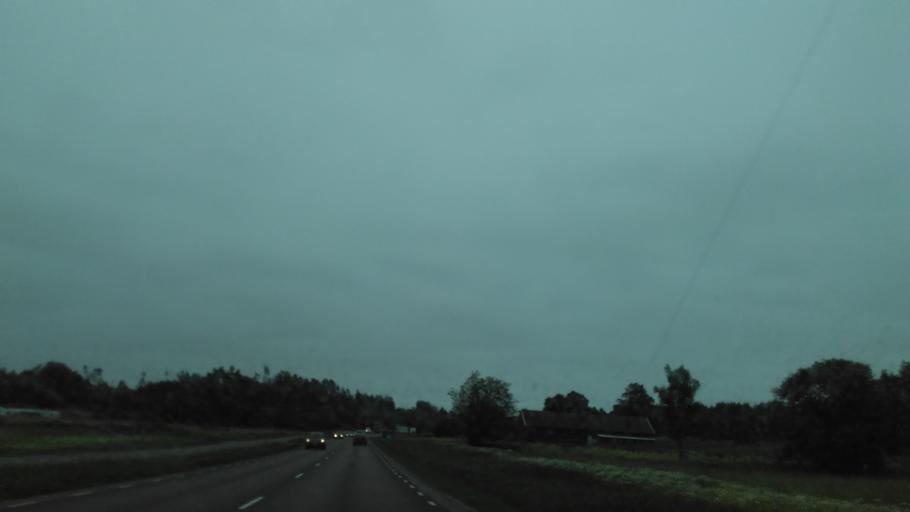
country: SE
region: Vaestra Goetaland
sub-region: Alingsas Kommun
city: Alingsas
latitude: 57.9400
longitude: 12.5841
